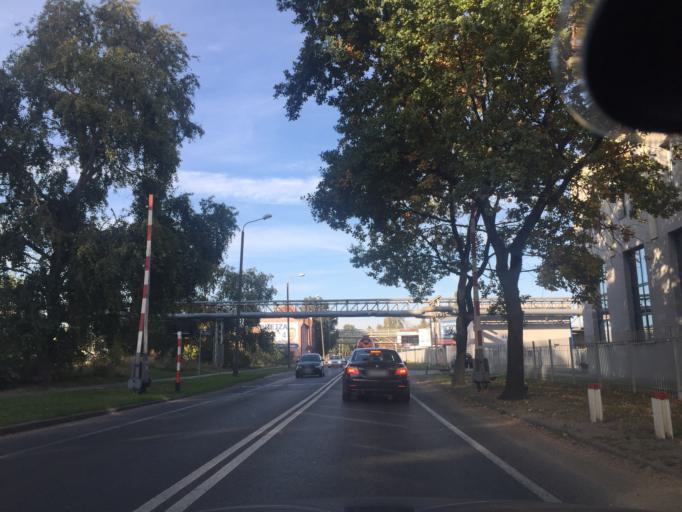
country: PL
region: Kujawsko-Pomorskie
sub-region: Powiat inowroclawski
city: Inowroclaw
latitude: 52.7492
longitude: 18.2555
